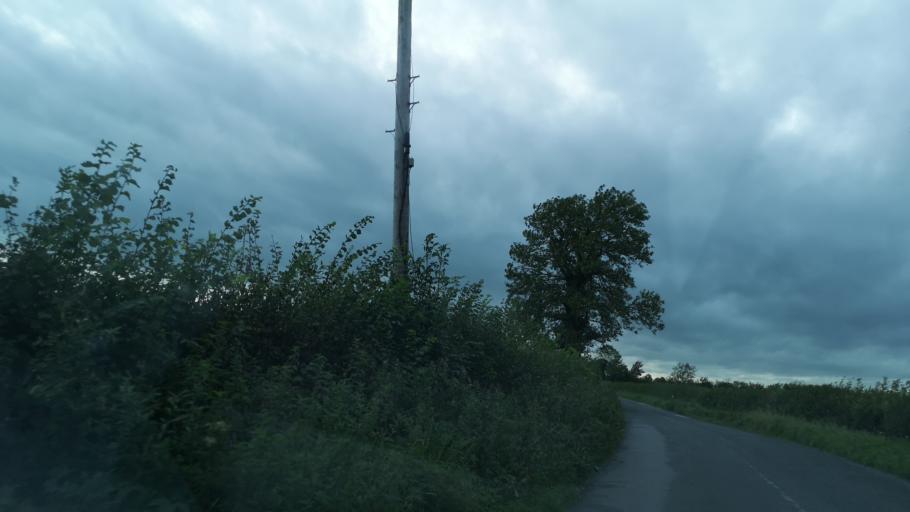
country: IE
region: Leinster
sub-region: Uibh Fhaili
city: Ferbane
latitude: 53.2217
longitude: -7.8069
